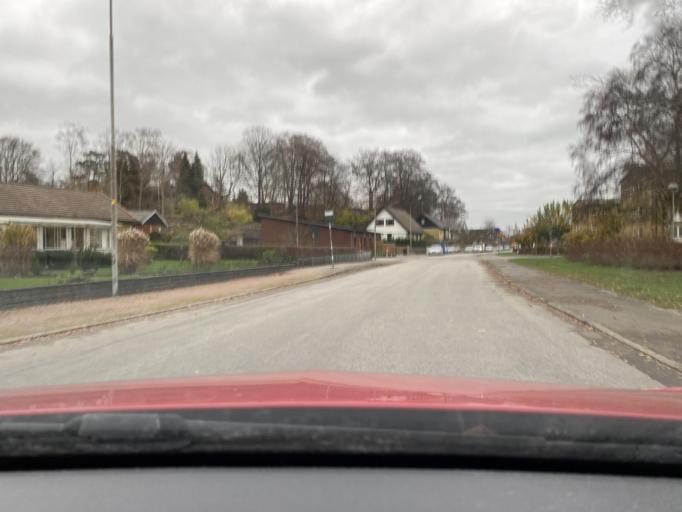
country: SE
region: Skane
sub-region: Hassleholms Kommun
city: Hassleholm
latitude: 56.1605
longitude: 13.7490
